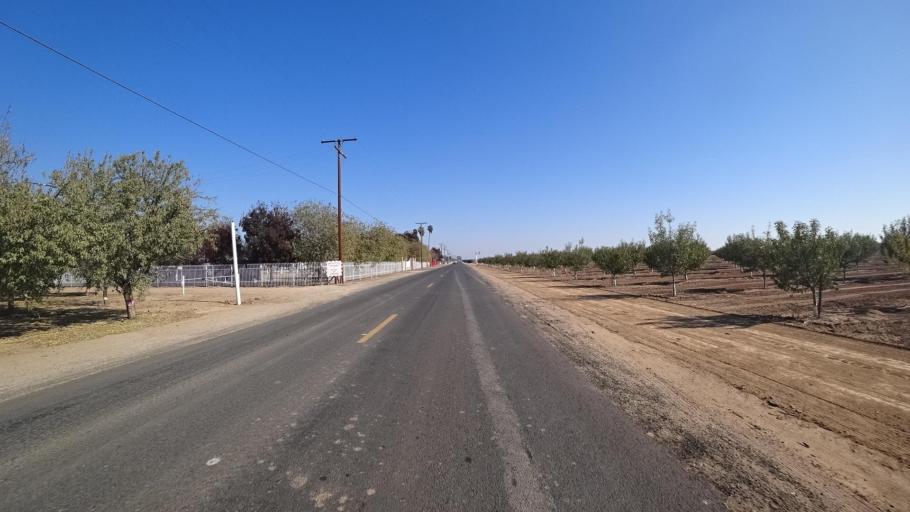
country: US
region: California
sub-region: Kern County
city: McFarland
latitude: 35.6890
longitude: -119.2165
